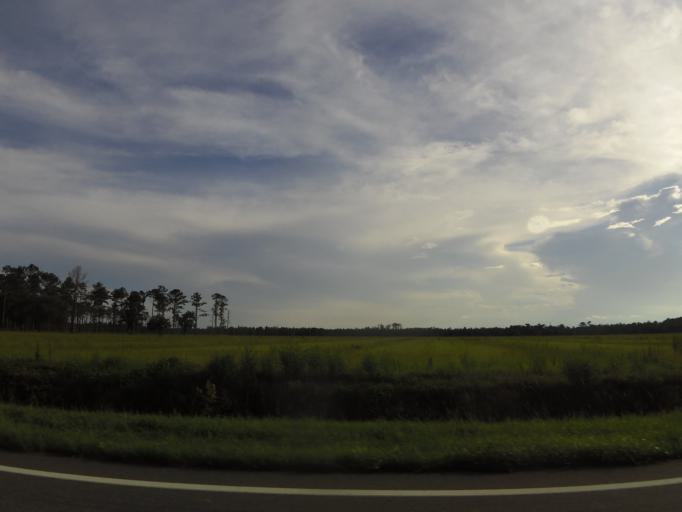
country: US
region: Florida
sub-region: Clay County
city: Green Cove Springs
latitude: 30.0057
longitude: -81.5503
